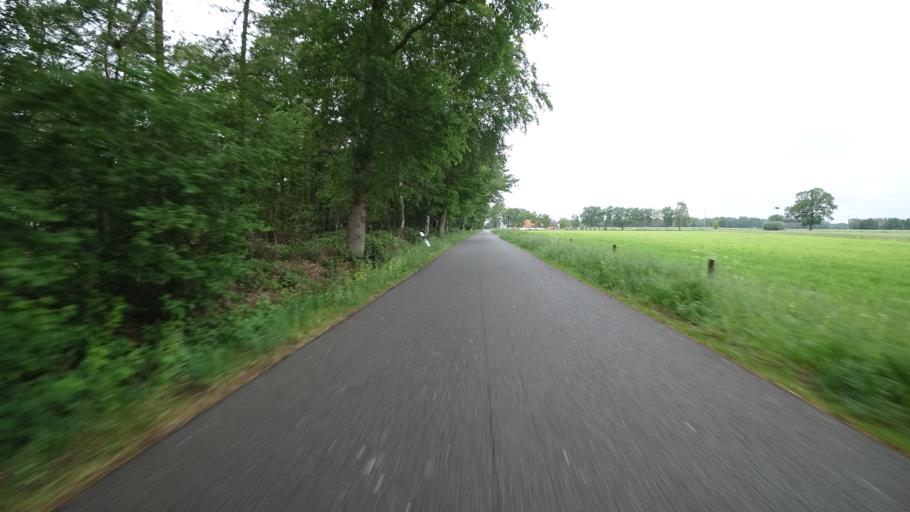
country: DE
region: North Rhine-Westphalia
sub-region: Regierungsbezirk Detmold
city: Rheda-Wiedenbruck
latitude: 51.8440
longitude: 8.3425
